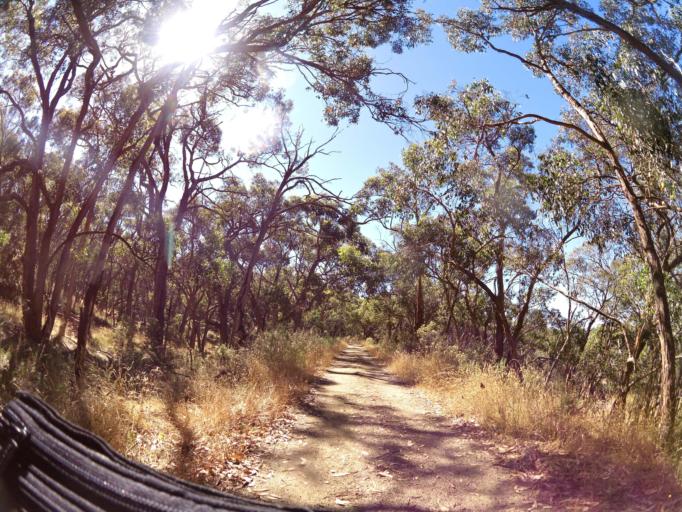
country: AU
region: Victoria
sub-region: Ballarat North
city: Delacombe
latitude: -37.6651
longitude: 143.5066
